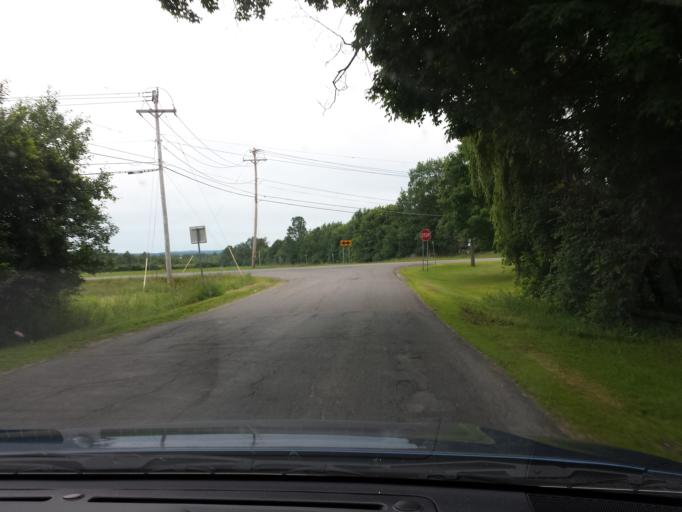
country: US
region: New York
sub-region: St. Lawrence County
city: Potsdam
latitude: 44.6848
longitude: -74.9619
